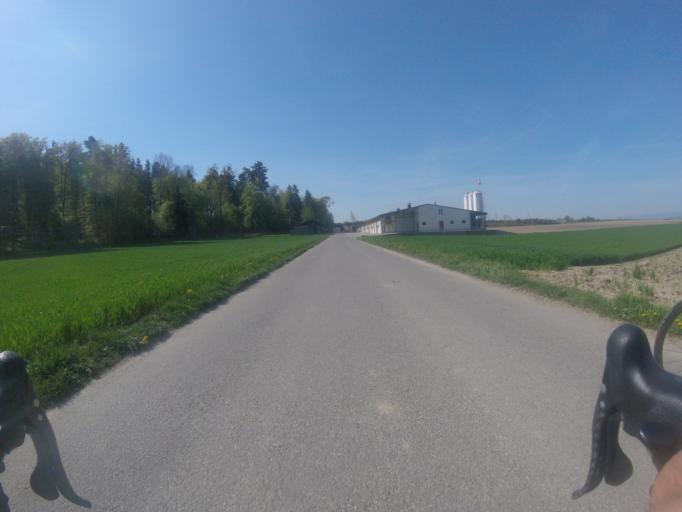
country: CH
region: Bern
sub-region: Bern-Mittelland District
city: Muhleberg
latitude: 46.9661
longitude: 7.2401
